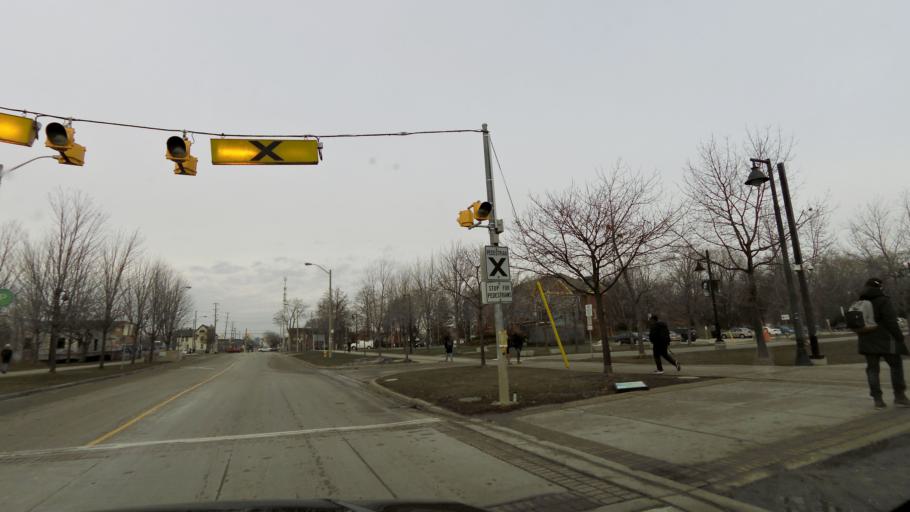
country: CA
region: Ontario
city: Etobicoke
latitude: 43.5967
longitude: -79.5162
